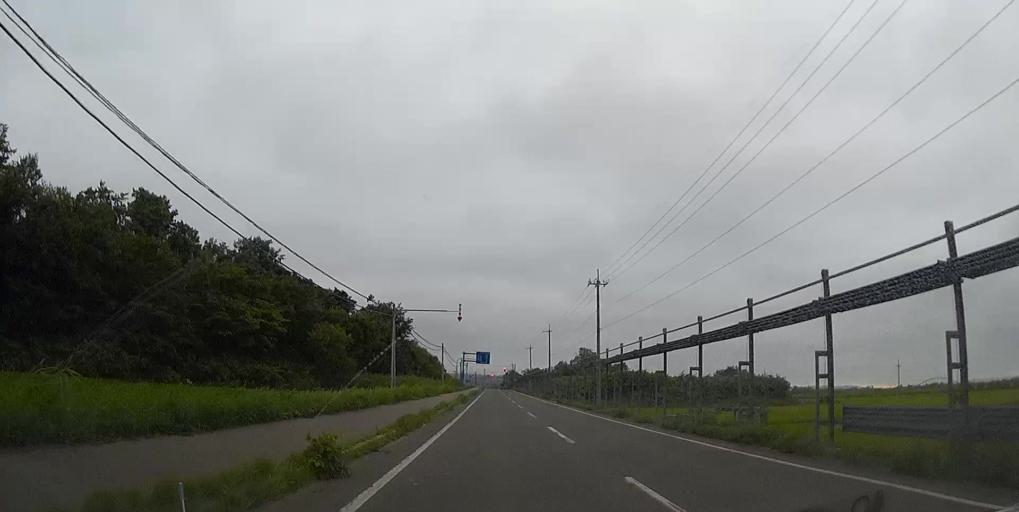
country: JP
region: Hokkaido
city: Iwanai
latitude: 42.4131
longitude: 140.0052
